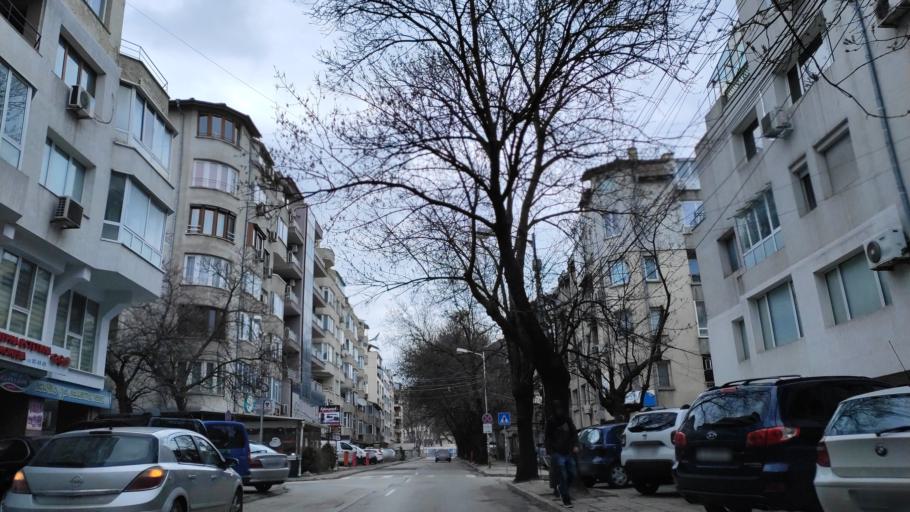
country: BG
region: Varna
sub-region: Obshtina Varna
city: Varna
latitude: 43.2159
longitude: 27.9174
